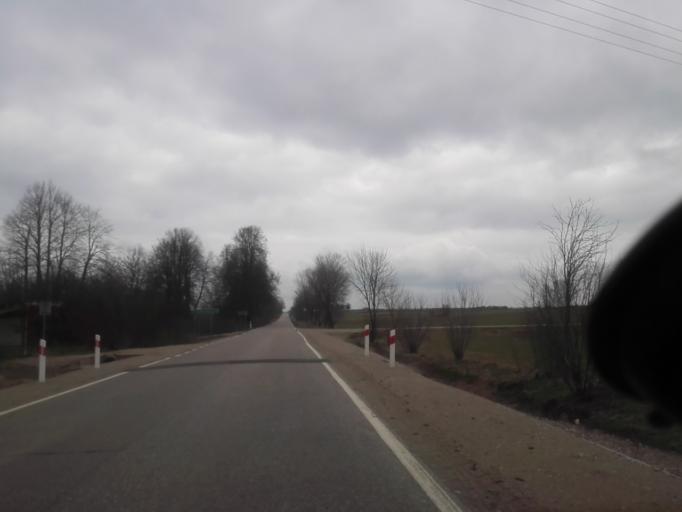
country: PL
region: Podlasie
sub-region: Suwalki
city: Suwalki
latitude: 54.2421
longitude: 22.9159
